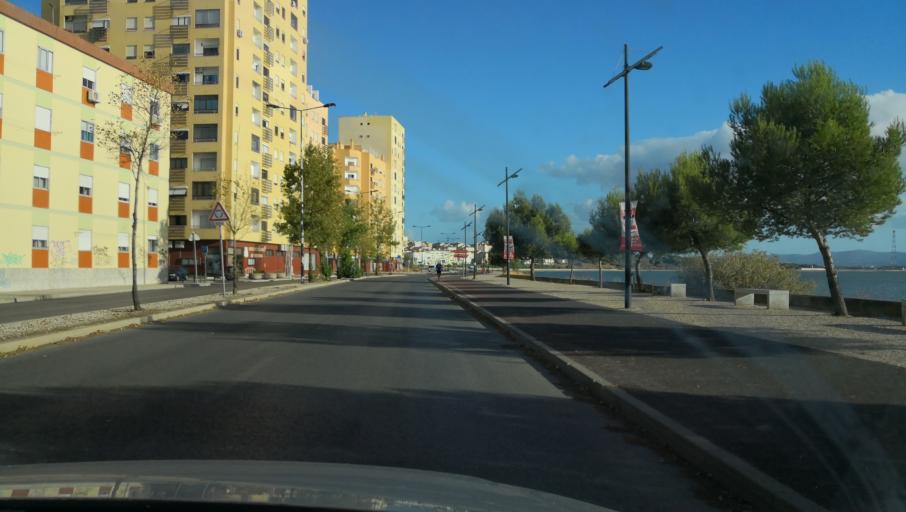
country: PT
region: Setubal
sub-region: Barreiro
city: Barreiro
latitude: 38.6520
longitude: -9.0721
